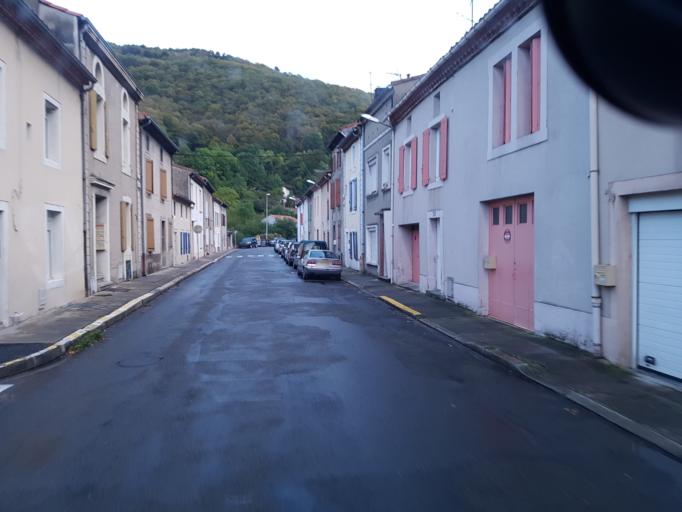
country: FR
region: Midi-Pyrenees
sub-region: Departement du Tarn
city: Mazamet
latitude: 43.4832
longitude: 2.3749
